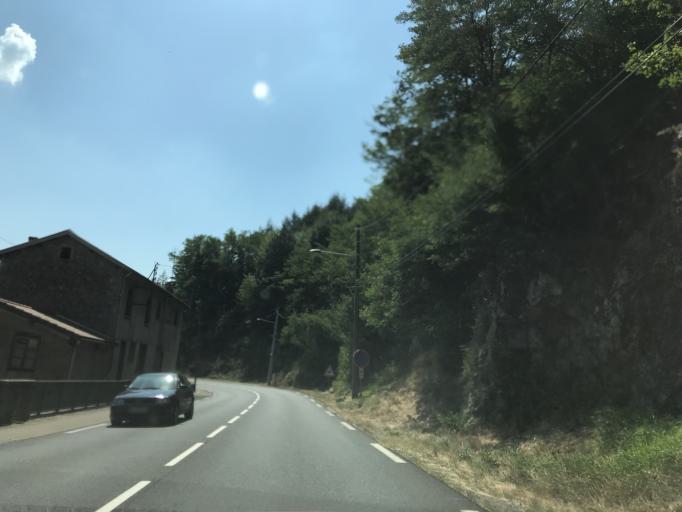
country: FR
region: Auvergne
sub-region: Departement du Puy-de-Dome
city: La Monnerie-le-Montel
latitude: 45.8680
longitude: 3.5922
